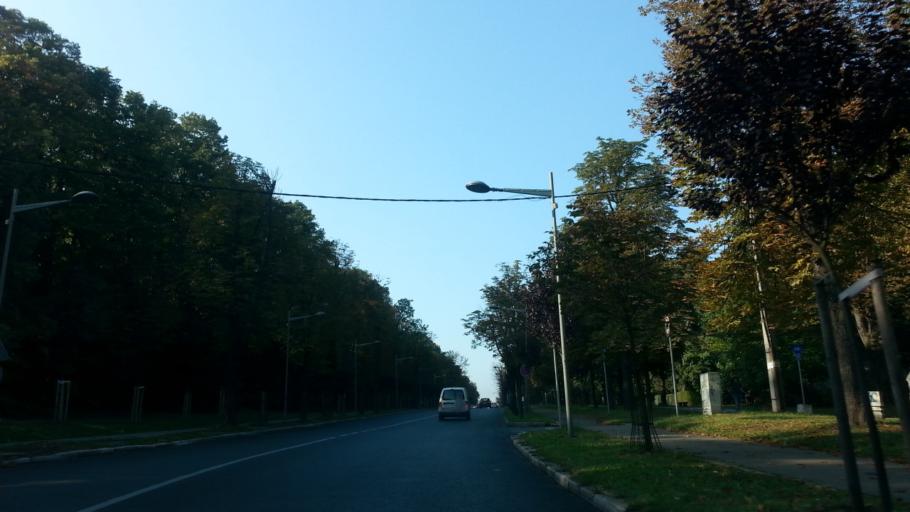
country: RS
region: Central Serbia
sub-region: Belgrade
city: Savski Venac
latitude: 44.7932
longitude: 20.4476
